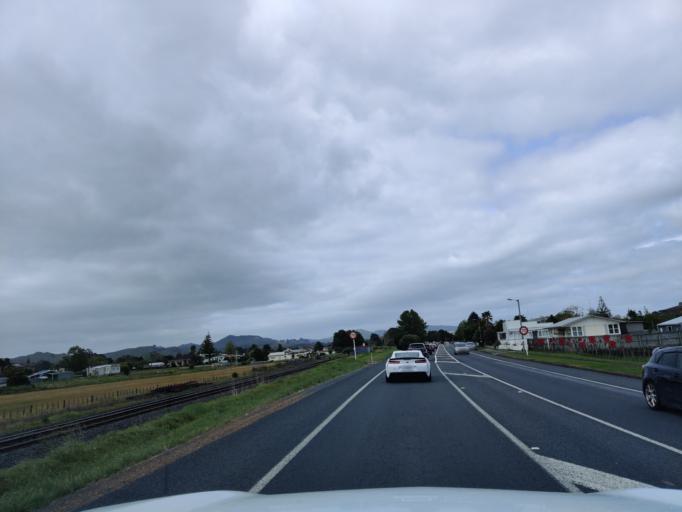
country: NZ
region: Waikato
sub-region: Waikato District
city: Ngaruawahia
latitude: -37.5342
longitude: 175.1592
